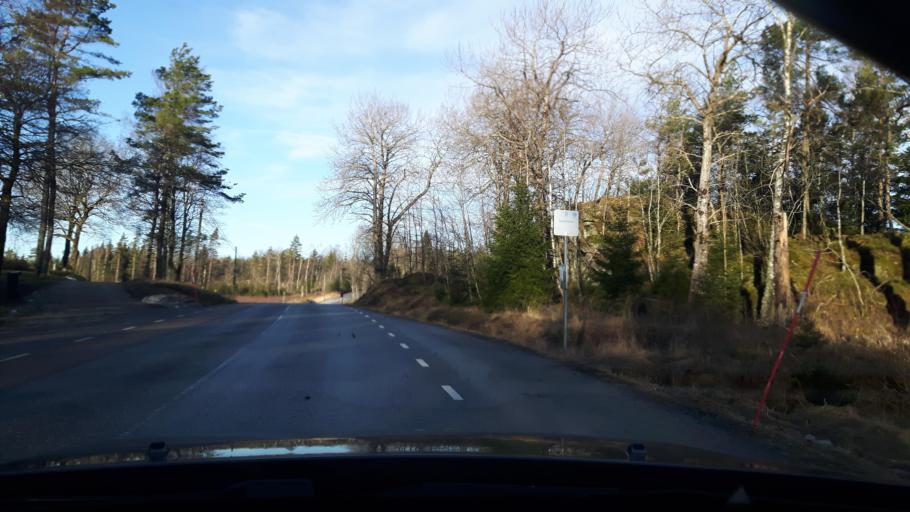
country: SE
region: Vaestra Goetaland
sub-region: Munkedals Kommun
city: Munkedal
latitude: 58.4972
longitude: 11.6926
